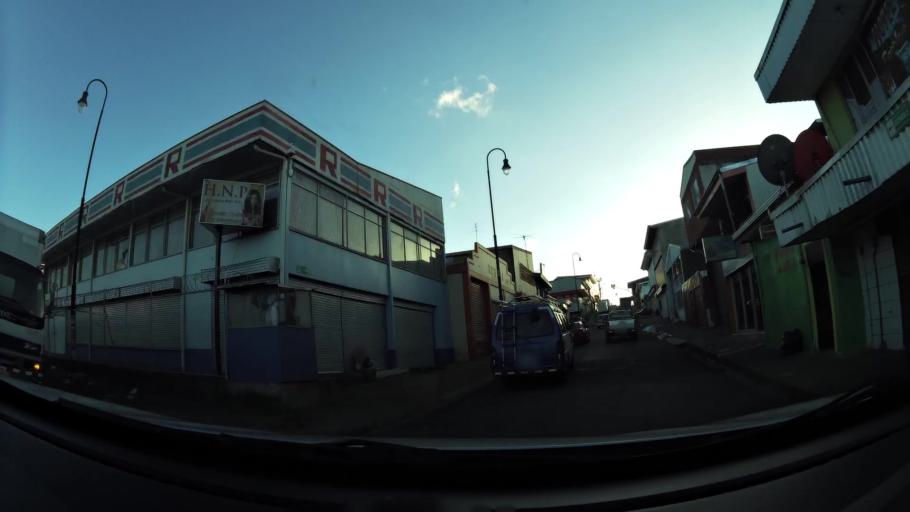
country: CR
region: San Jose
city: San Jose
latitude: 9.9376
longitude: -84.0847
